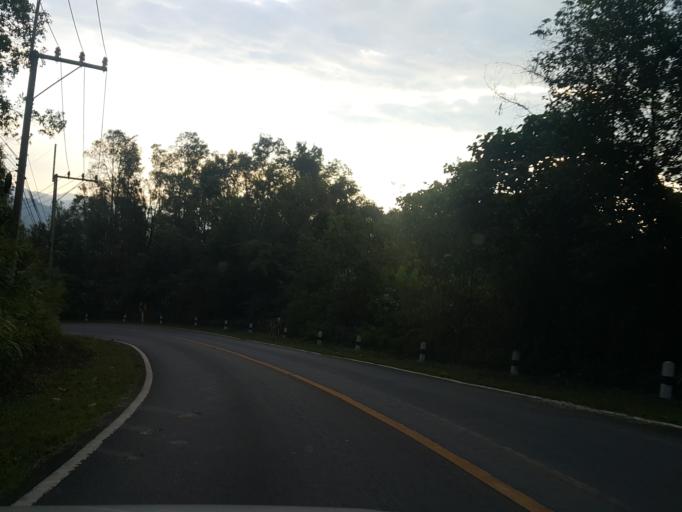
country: TH
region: Mae Hong Son
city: Khun Yuam
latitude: 18.8010
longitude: 98.0710
